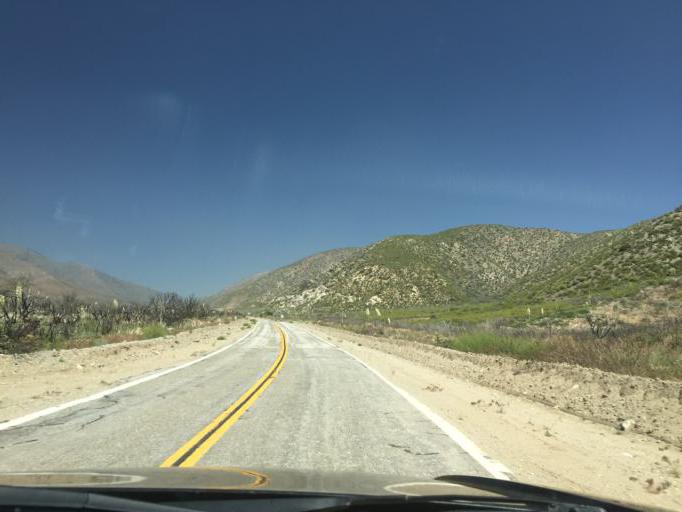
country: US
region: California
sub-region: San Bernardino County
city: Wrightwood
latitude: 34.3114
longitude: -117.5343
